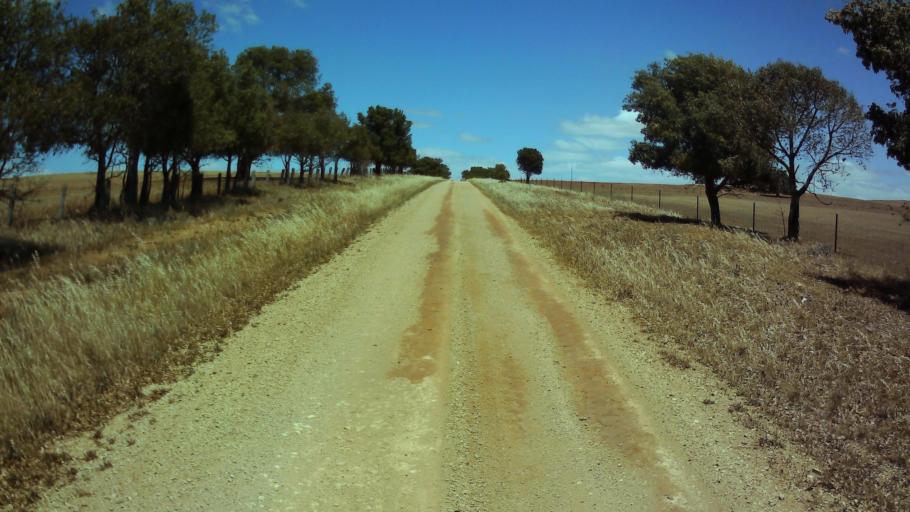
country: AU
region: New South Wales
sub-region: Weddin
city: Grenfell
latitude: -33.9461
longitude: 148.3703
